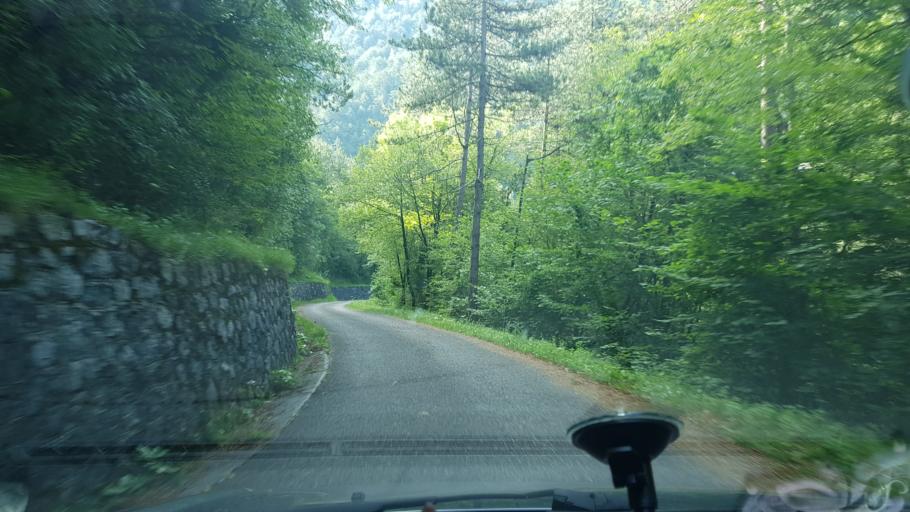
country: IT
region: Friuli Venezia Giulia
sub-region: Provincia di Udine
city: Prato
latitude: 46.3579
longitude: 13.3611
